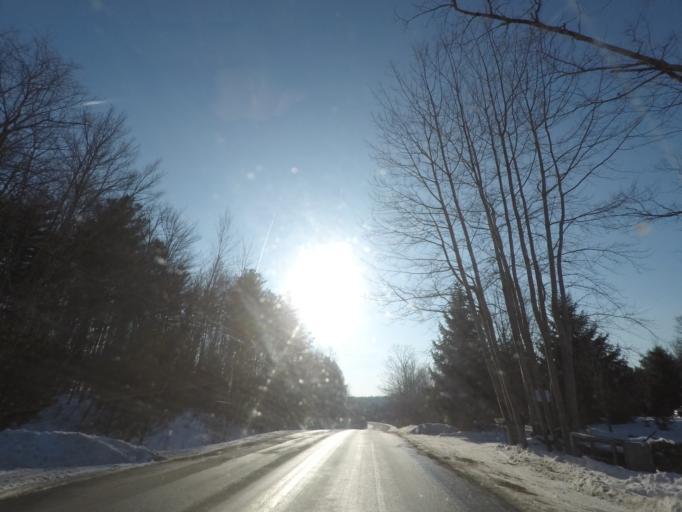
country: US
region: Massachusetts
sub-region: Berkshire County
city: Richmond
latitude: 42.5302
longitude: -73.4088
